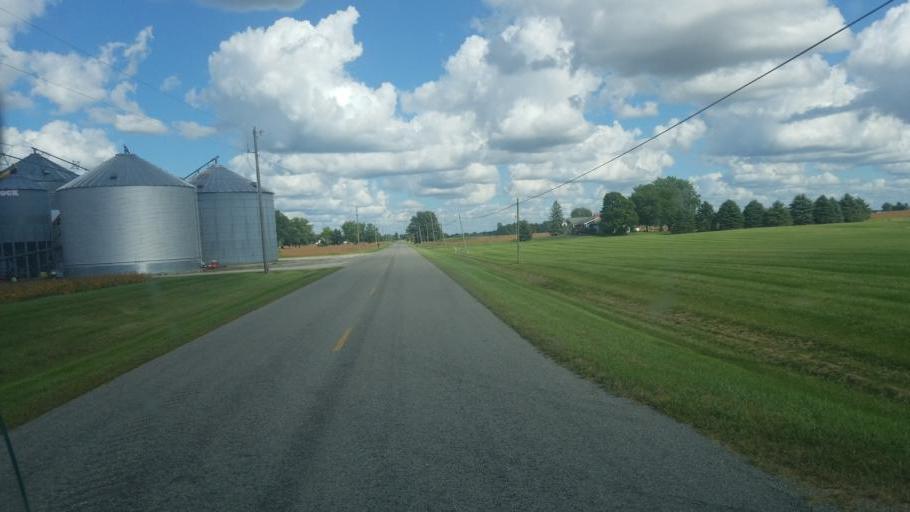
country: US
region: Ohio
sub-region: Hardin County
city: Kenton
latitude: 40.5051
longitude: -83.5869
